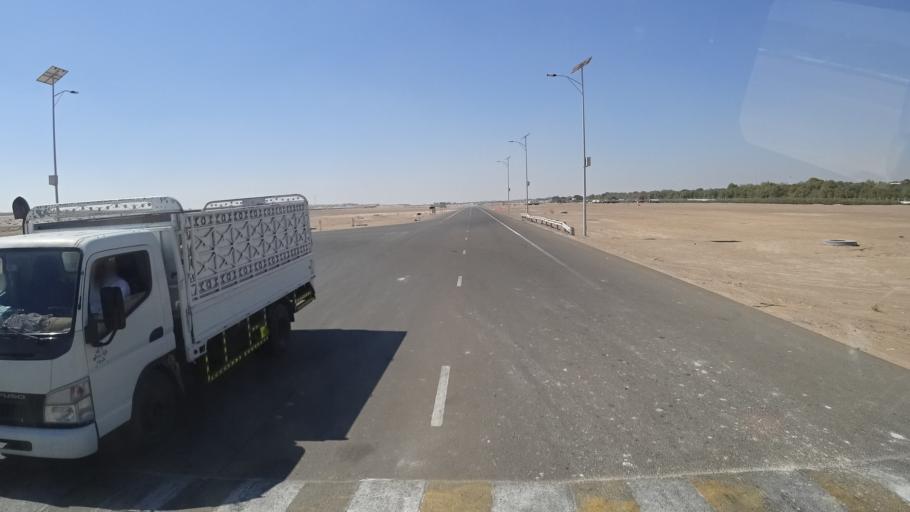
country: AE
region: Abu Dhabi
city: Abu Dhabi
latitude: 24.2115
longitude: 54.6988
